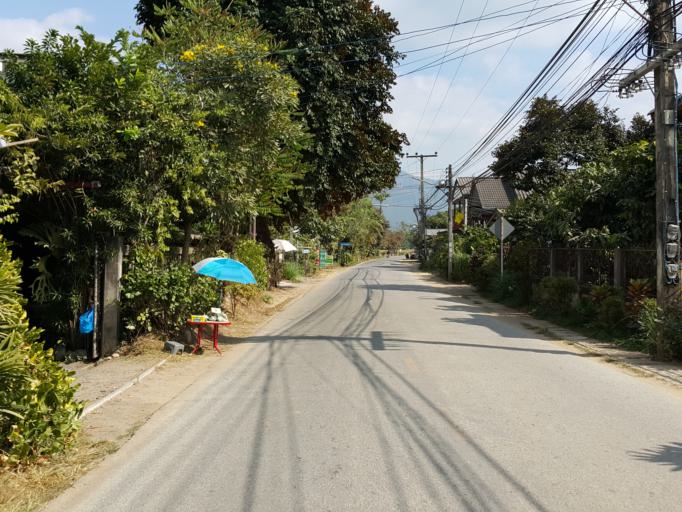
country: TH
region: Chiang Mai
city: Mae On
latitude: 18.7252
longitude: 99.1988
